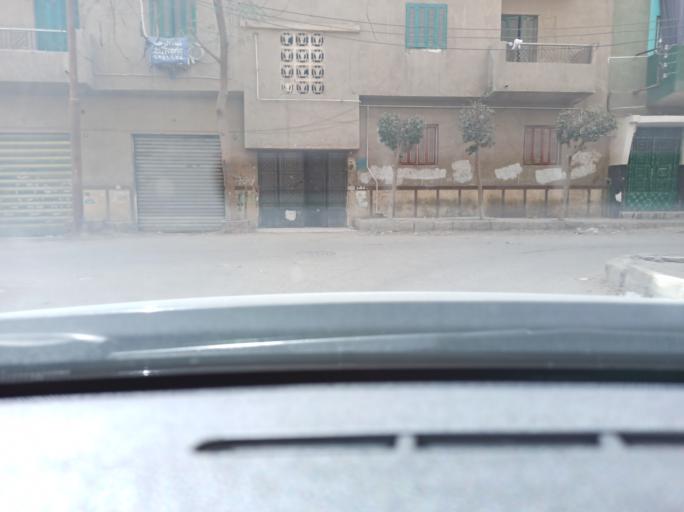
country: EG
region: Muhafazat Bani Suwayf
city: Bani Suwayf
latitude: 29.0814
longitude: 31.0883
